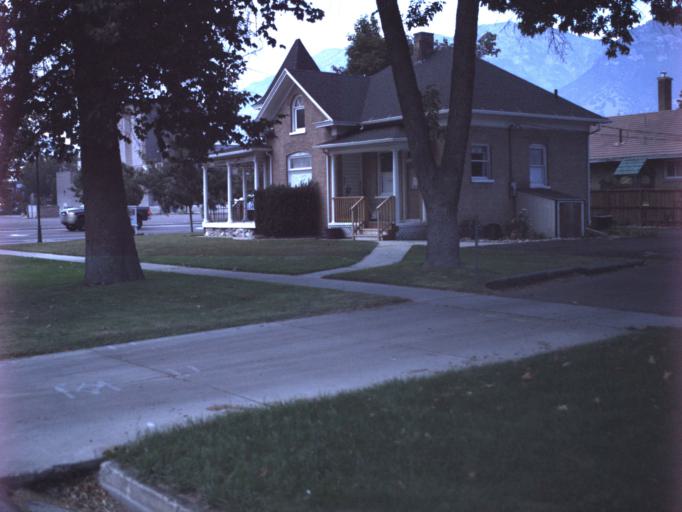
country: US
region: Utah
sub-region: Utah County
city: Provo
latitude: 40.2319
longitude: -111.6674
